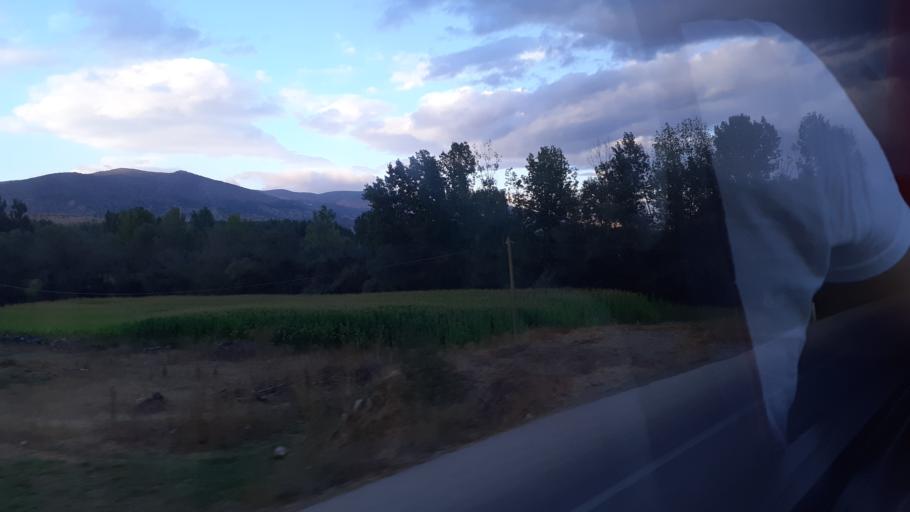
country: TR
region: Tokat
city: Dokmetepe
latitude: 40.3223
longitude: 36.2243
